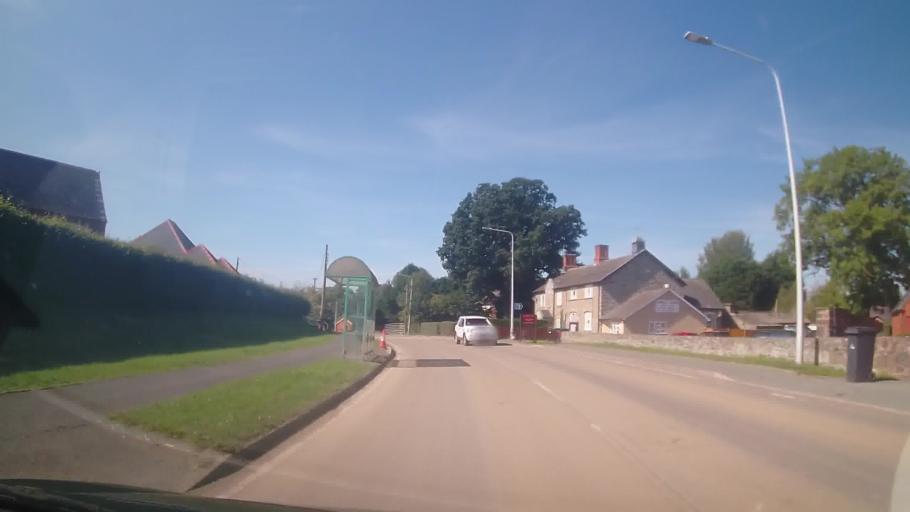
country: GB
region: England
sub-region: Shropshire
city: Mainstone
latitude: 52.5390
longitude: -3.0726
